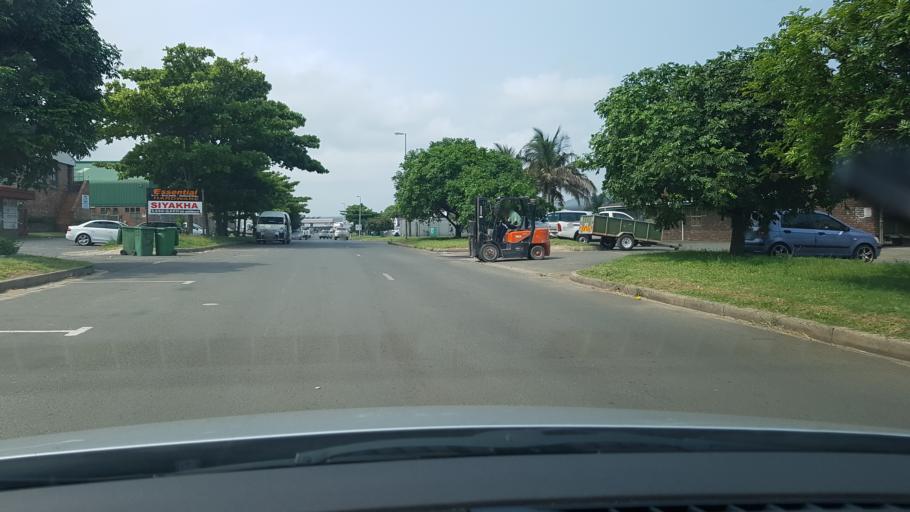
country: ZA
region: KwaZulu-Natal
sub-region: uThungulu District Municipality
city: Richards Bay
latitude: -28.7469
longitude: 32.0476
